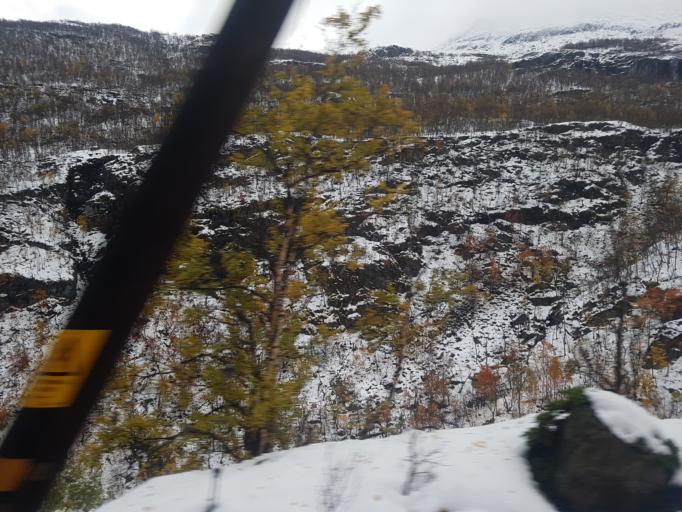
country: NO
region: Sor-Trondelag
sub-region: Oppdal
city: Oppdal
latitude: 62.3621
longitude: 9.6330
